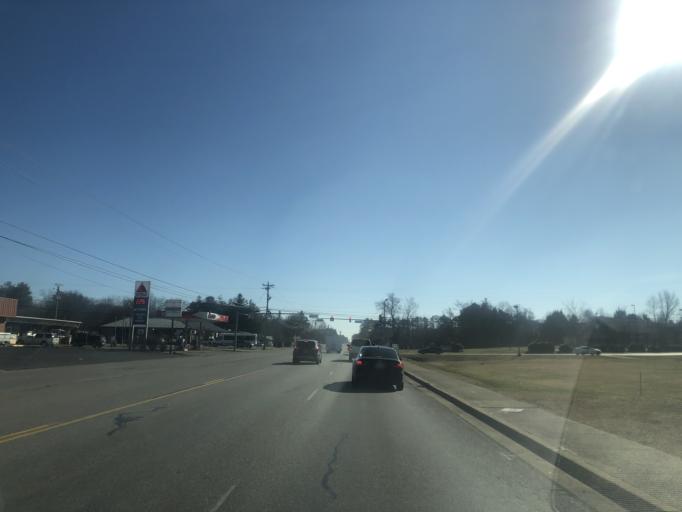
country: US
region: Tennessee
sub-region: Rutherford County
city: Smyrna
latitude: 35.9485
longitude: -86.5086
